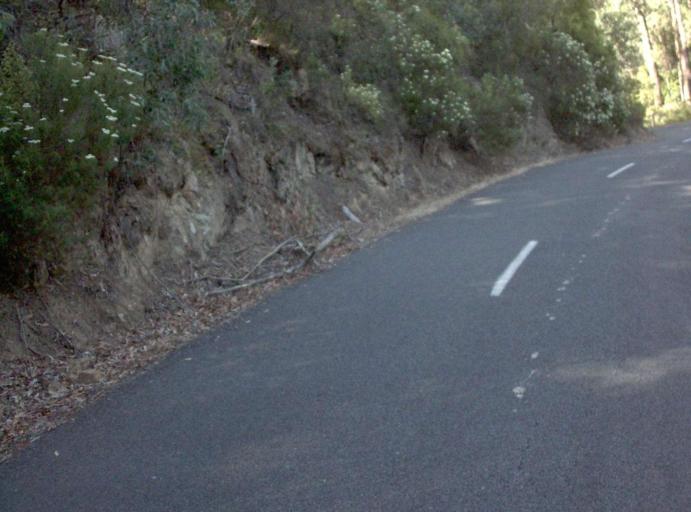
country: AU
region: Victoria
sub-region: East Gippsland
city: Lakes Entrance
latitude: -37.4544
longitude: 148.5765
